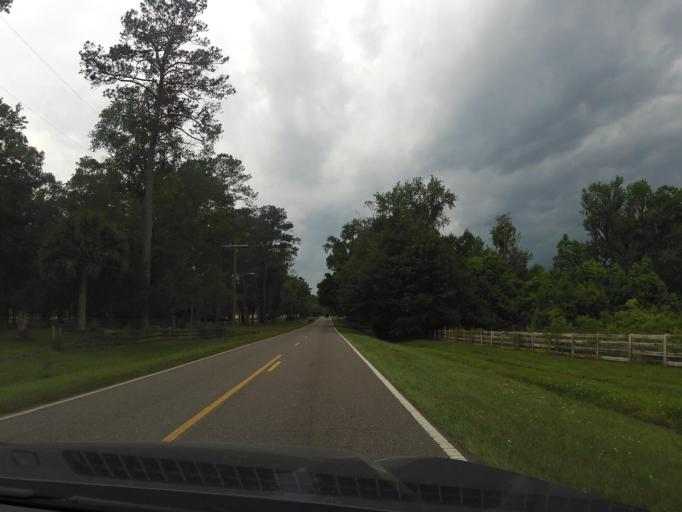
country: US
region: Florida
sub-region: Duval County
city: Jacksonville
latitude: 30.3462
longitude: -81.8006
